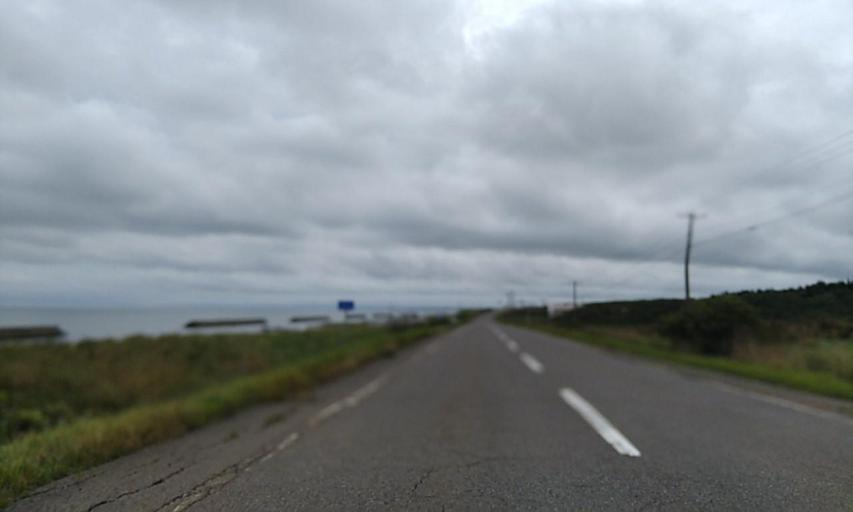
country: JP
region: Hokkaido
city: Shibetsu
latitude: 43.4325
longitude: 145.2635
